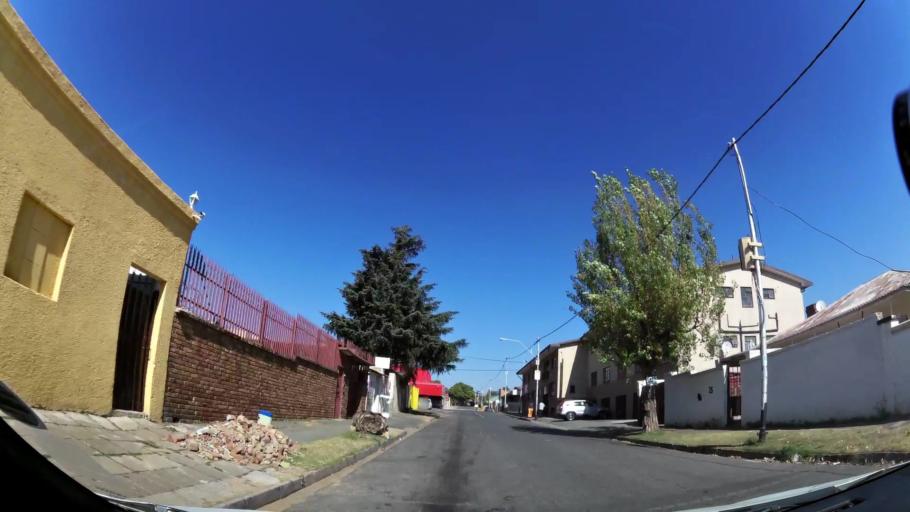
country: ZA
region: Gauteng
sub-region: City of Johannesburg Metropolitan Municipality
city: Johannesburg
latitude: -26.2399
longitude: 28.0665
